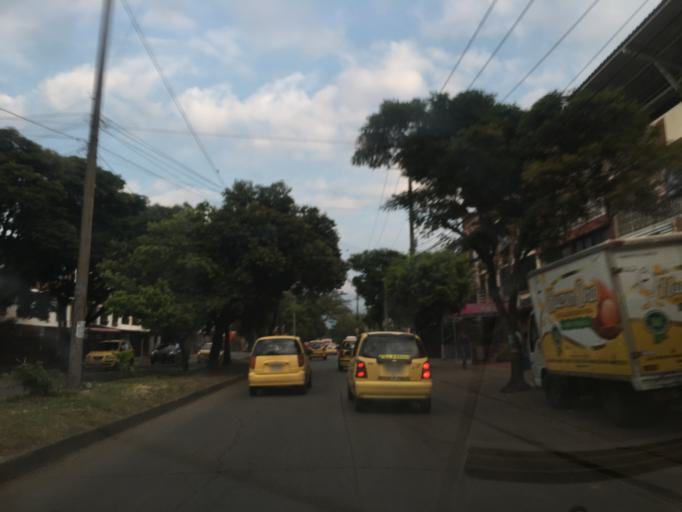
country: CO
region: Valle del Cauca
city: Cali
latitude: 3.4021
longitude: -76.5259
